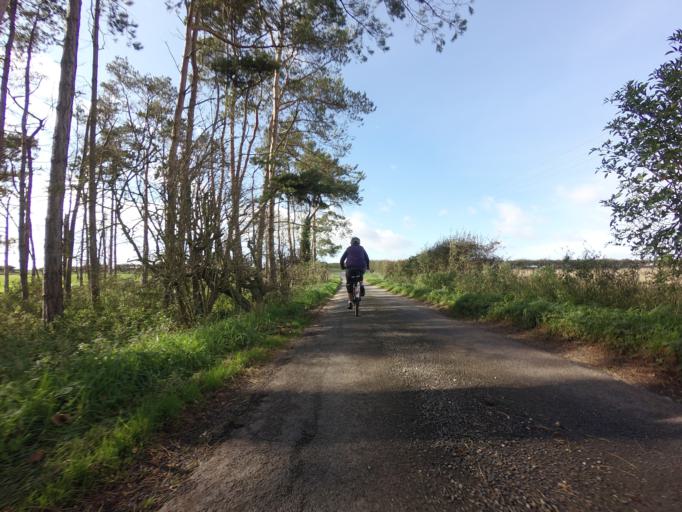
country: GB
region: England
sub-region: Norfolk
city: Hunstanton
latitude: 52.9363
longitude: 0.6271
